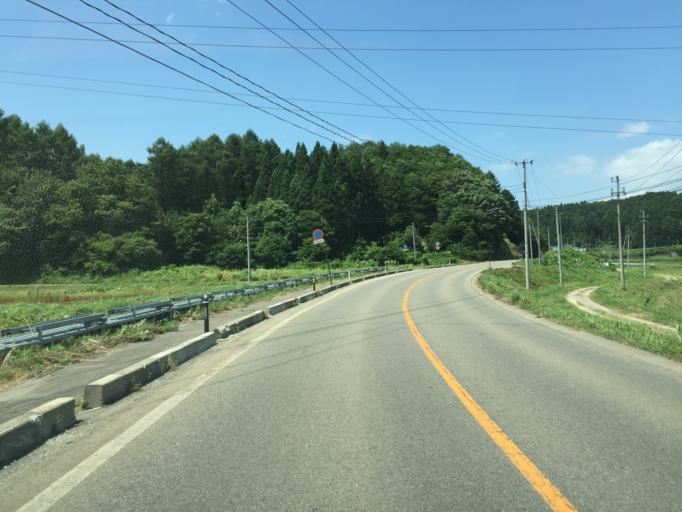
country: JP
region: Fukushima
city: Inawashiro
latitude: 37.5000
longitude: 139.9970
